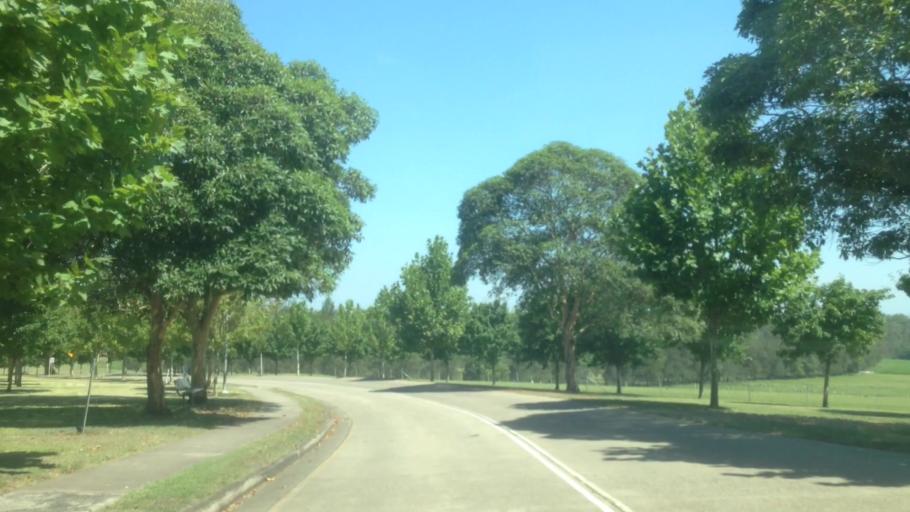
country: AU
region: New South Wales
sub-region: Lake Macquarie Shire
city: Cooranbong
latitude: -33.0823
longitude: 151.4559
